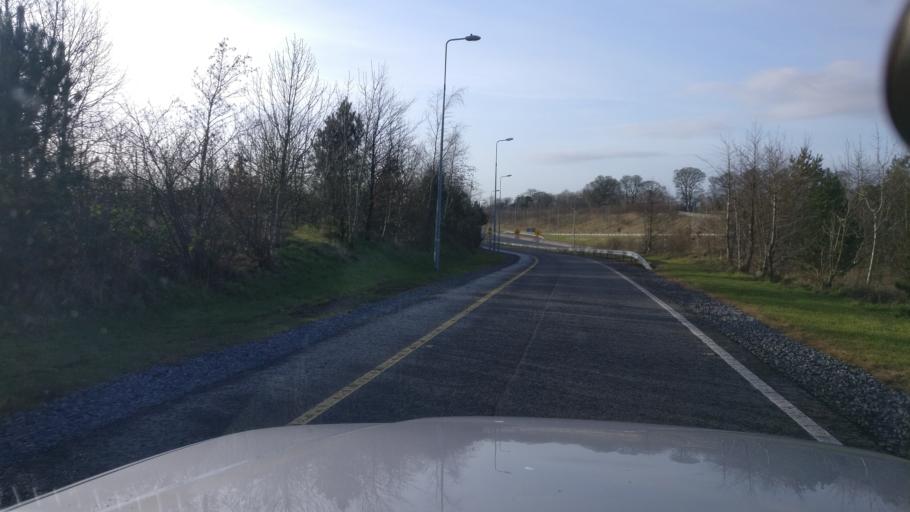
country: IE
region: Leinster
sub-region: An Iarmhi
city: Moate
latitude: 53.3861
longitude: -7.6838
